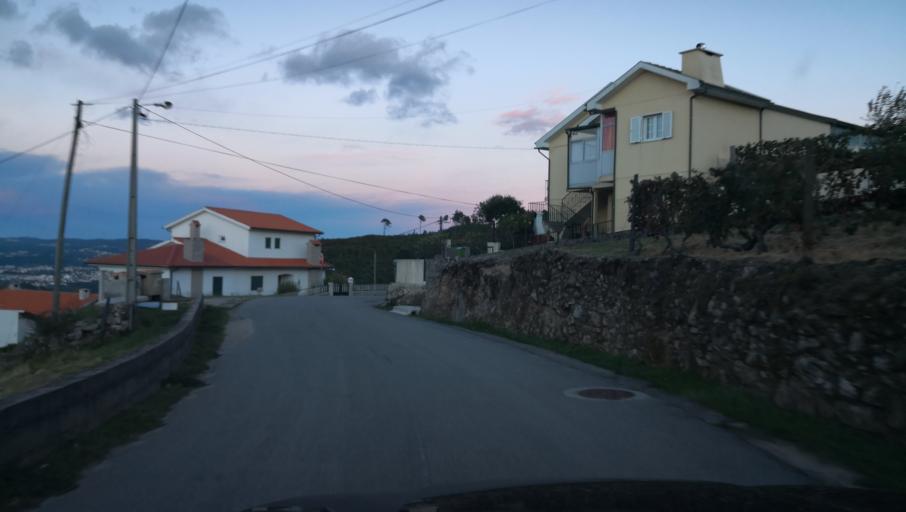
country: PT
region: Vila Real
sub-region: Santa Marta de Penaguiao
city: Santa Marta de Penaguiao
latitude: 41.2634
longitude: -7.7920
